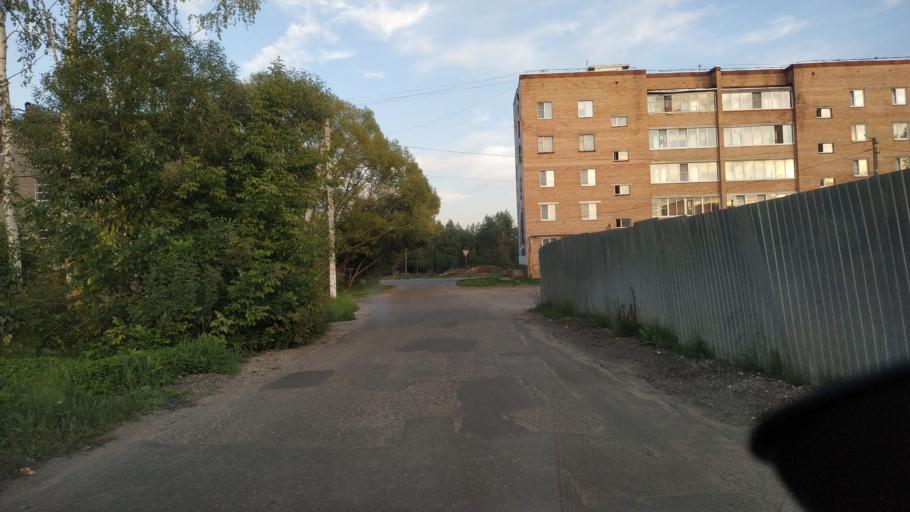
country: RU
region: Moskovskaya
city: Roshal'
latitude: 55.6624
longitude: 39.8564
